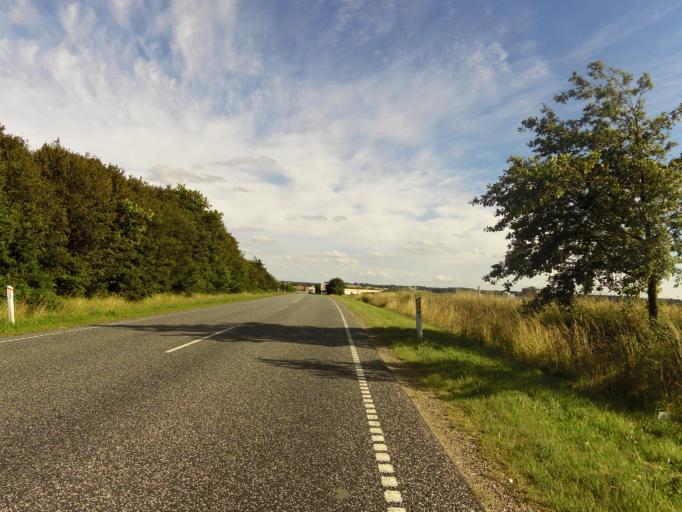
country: DK
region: South Denmark
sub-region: Tonder Kommune
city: Toftlund
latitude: 55.1834
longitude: 9.0598
